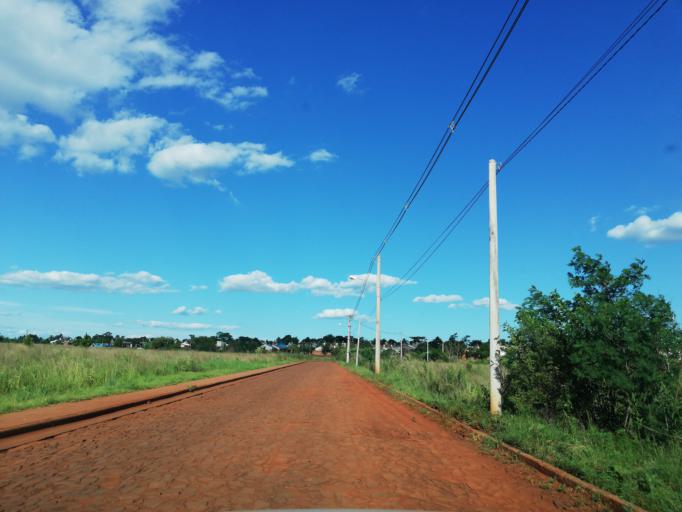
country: AR
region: Misiones
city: Garupa
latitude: -27.4664
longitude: -55.8809
